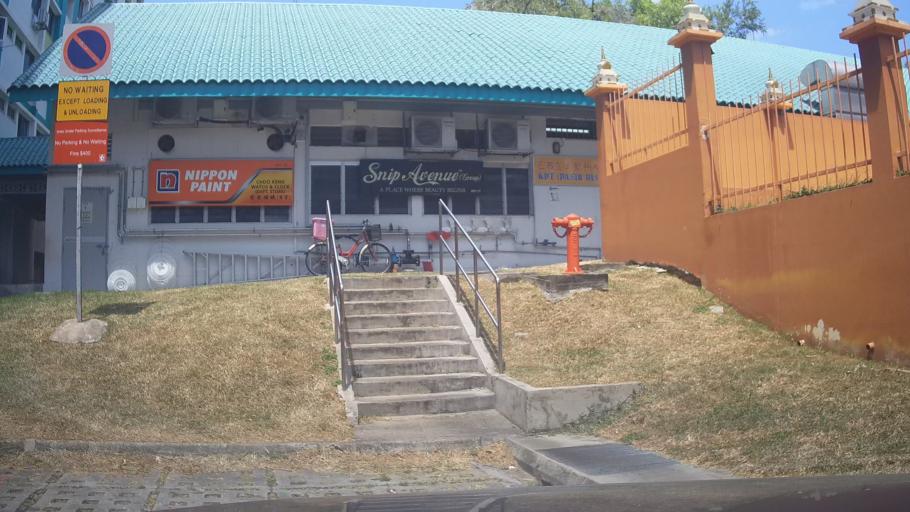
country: MY
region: Johor
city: Kampung Pasir Gudang Baru
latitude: 1.3690
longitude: 103.9588
